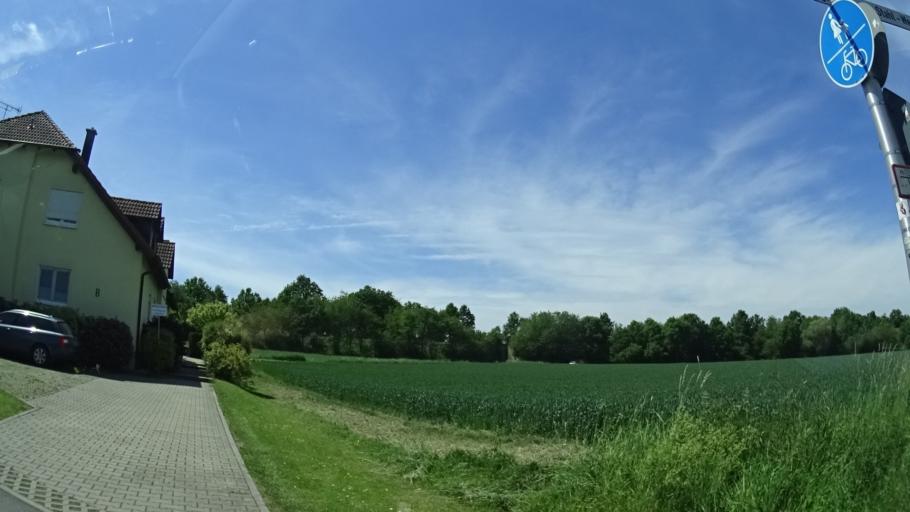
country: DE
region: Bavaria
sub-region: Regierungsbezirk Unterfranken
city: Poppenhausen
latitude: 50.0876
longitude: 10.1413
